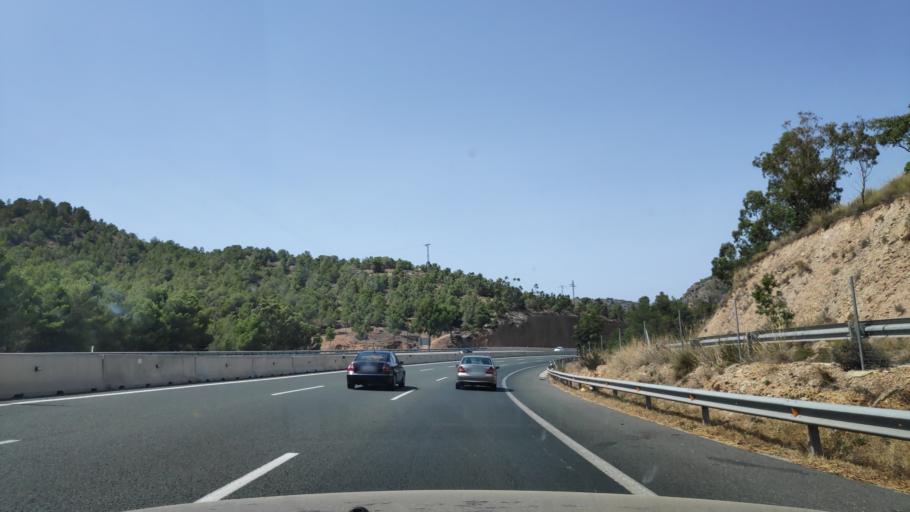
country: ES
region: Murcia
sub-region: Murcia
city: Murcia
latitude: 37.8919
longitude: -1.1422
